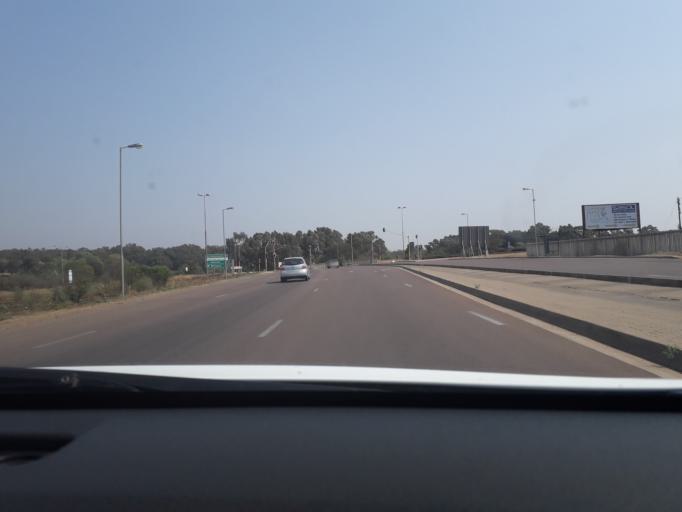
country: ZA
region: Gauteng
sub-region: City of Tshwane Metropolitan Municipality
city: Centurion
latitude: -25.9184
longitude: 28.2276
